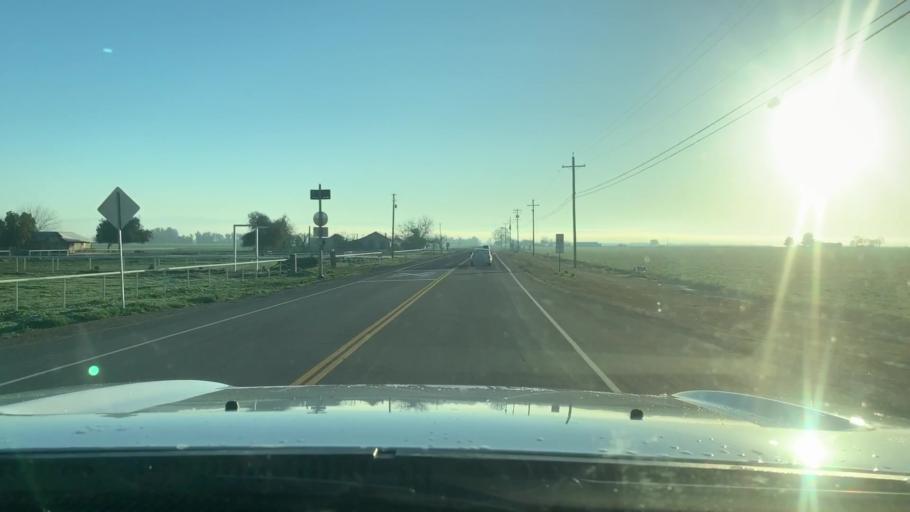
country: US
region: California
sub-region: Kings County
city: Home Garden
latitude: 36.2113
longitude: -119.6367
